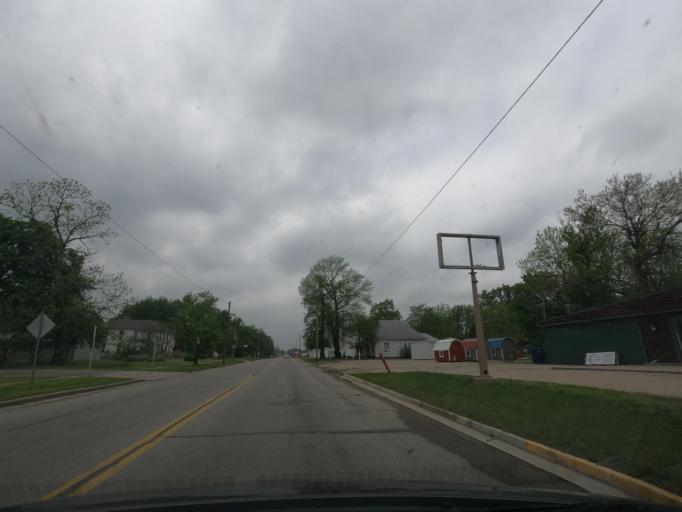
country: US
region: Kansas
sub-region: Cherokee County
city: Columbus
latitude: 37.1709
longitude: -94.8332
